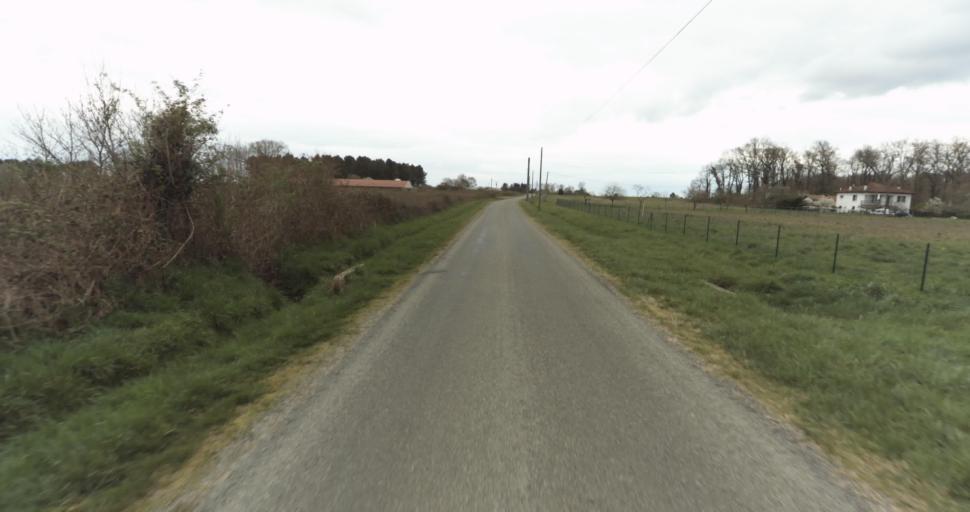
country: FR
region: Aquitaine
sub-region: Departement des Landes
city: Roquefort
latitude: 44.0181
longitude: -0.3327
